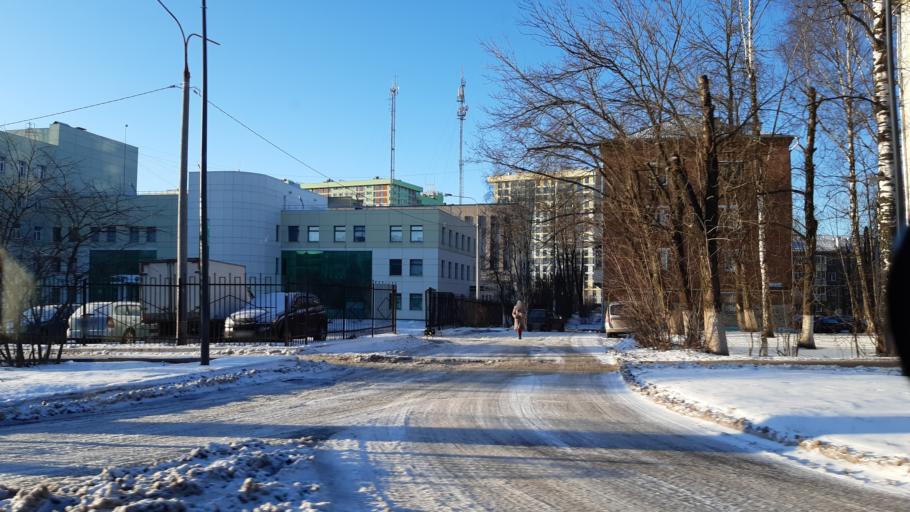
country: RU
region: Moskovskaya
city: Sergiyev Posad
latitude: 56.3231
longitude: 38.1454
